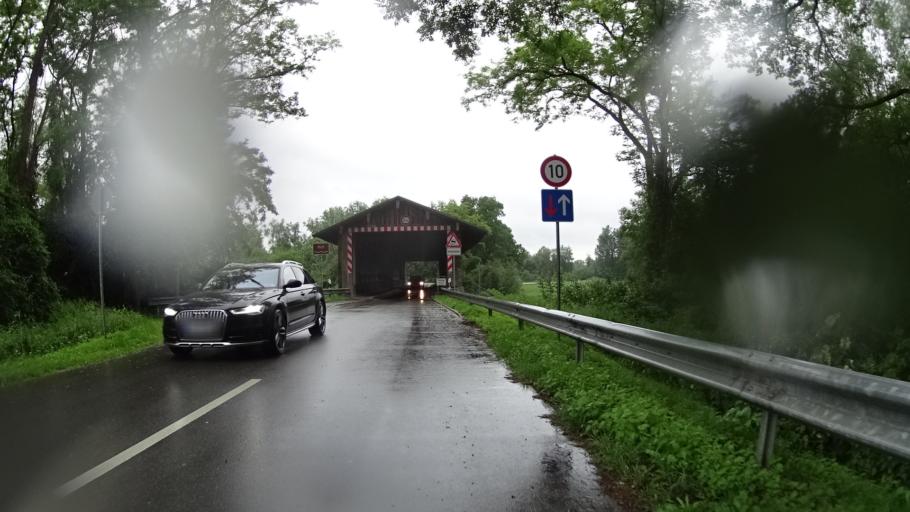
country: AT
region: Upper Austria
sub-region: Politischer Bezirk Scharding
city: Scharding
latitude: 48.4485
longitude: 13.4150
